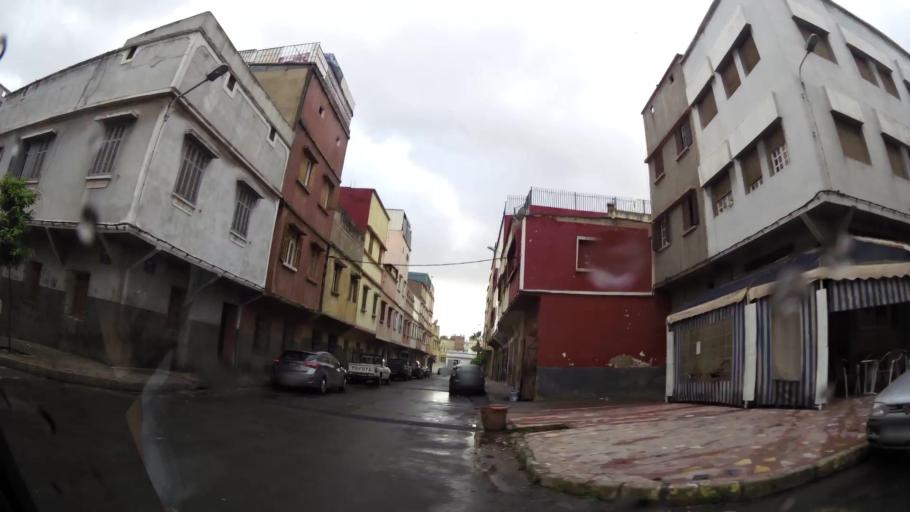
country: MA
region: Grand Casablanca
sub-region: Casablanca
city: Casablanca
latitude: 33.5502
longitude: -7.5822
